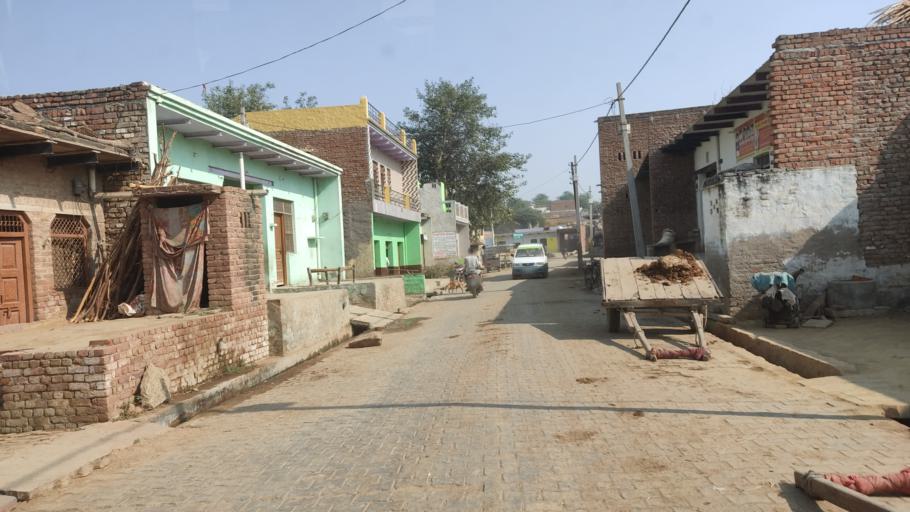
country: IN
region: Uttar Pradesh
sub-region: Mathura
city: Radha Kund
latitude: 27.5570
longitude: 77.5587
